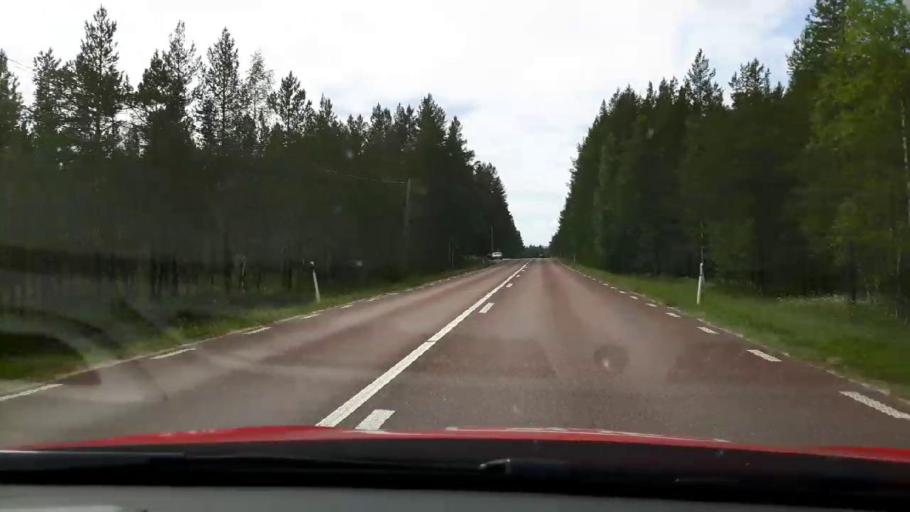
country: SE
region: Jaemtland
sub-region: Harjedalens Kommun
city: Sveg
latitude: 62.0589
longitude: 14.5720
